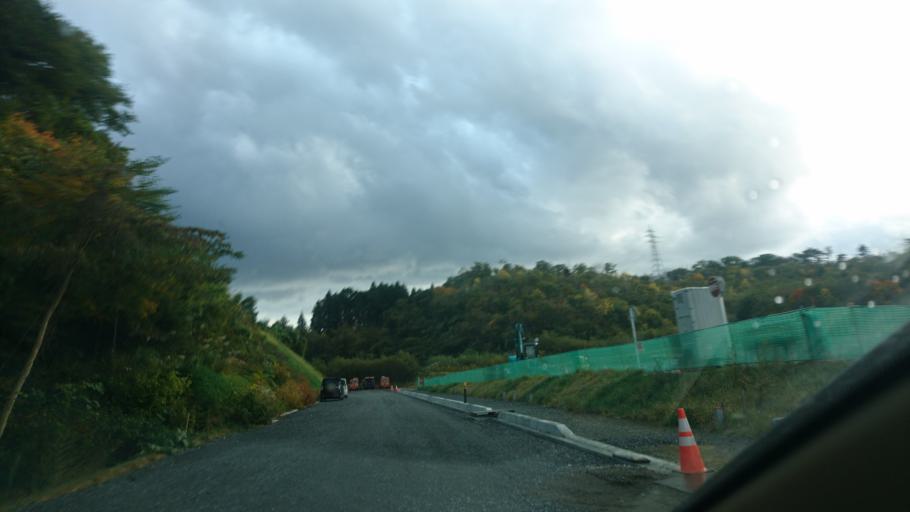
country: JP
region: Iwate
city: Ichinoseki
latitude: 38.9617
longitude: 141.1176
